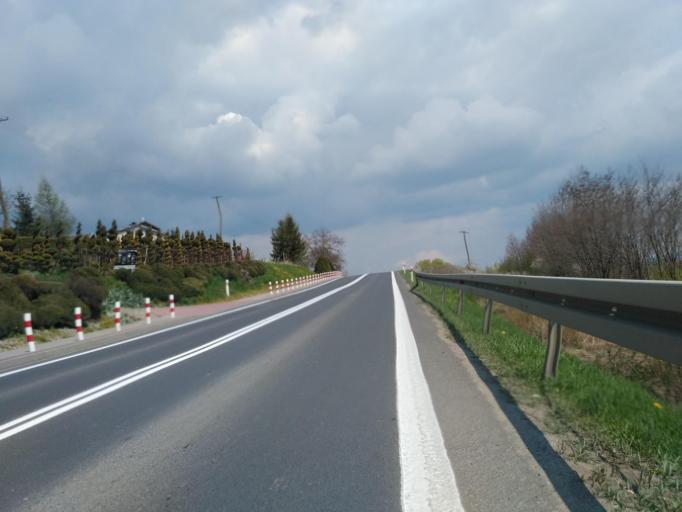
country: PL
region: Subcarpathian Voivodeship
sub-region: Powiat sanocki
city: Nowosielce-Gniewosz
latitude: 49.5591
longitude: 22.1140
